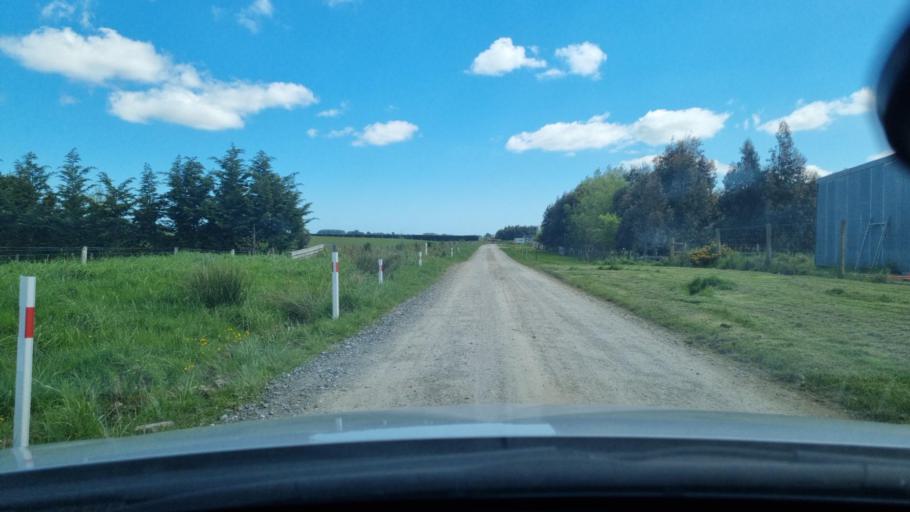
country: NZ
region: Southland
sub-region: Invercargill City
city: Invercargill
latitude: -46.3740
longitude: 168.3407
